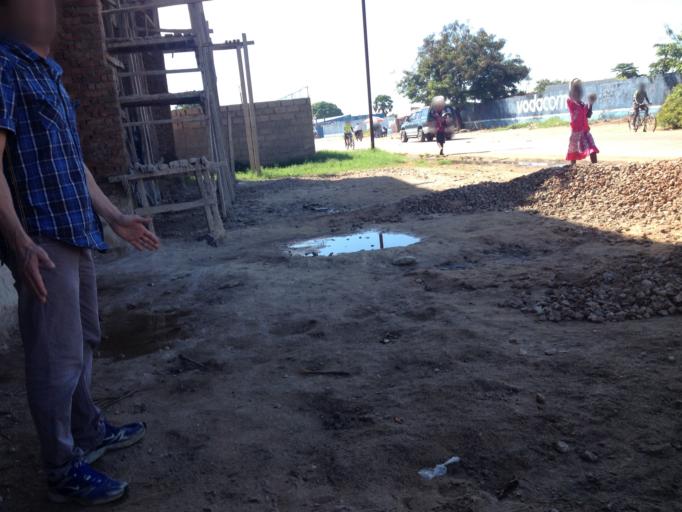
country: CD
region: Katanga
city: Kalemie
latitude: -5.9136
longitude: 29.2022
